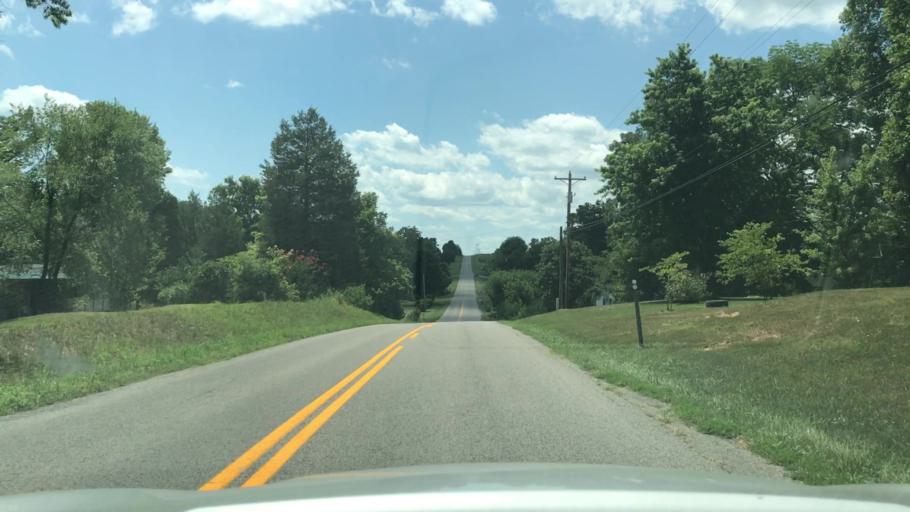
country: US
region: Kentucky
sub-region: Christian County
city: Hopkinsville
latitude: 36.9715
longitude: -87.3723
